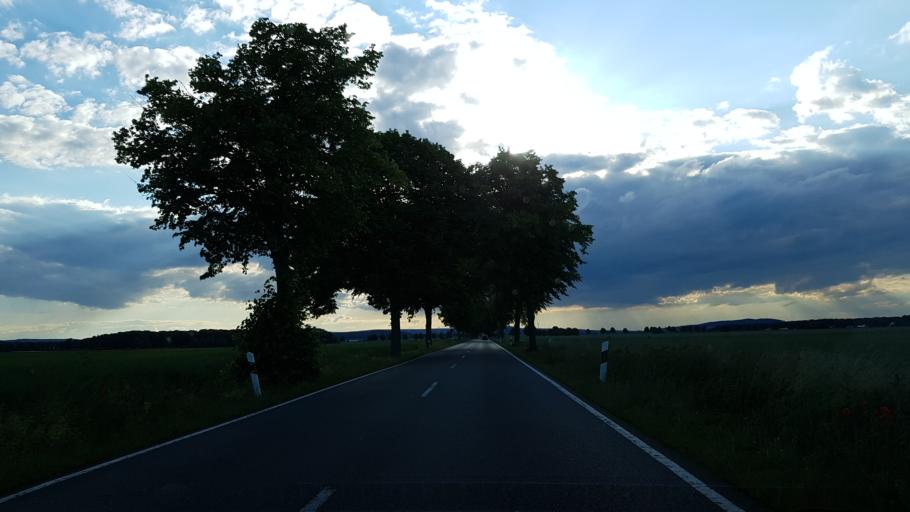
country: DE
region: Lower Saxony
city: Nordstemmen
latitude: 52.2055
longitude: 9.7651
